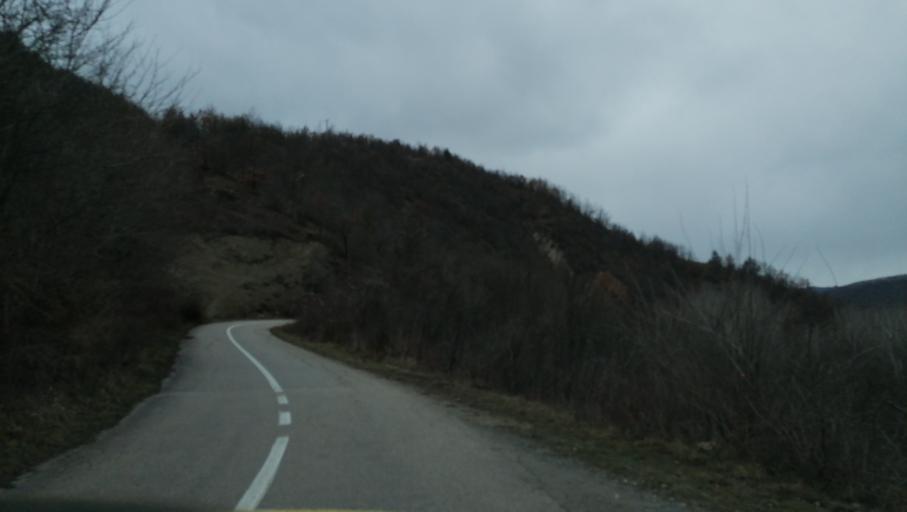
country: RS
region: Central Serbia
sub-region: Pirotski Okrug
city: Dimitrovgrad
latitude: 42.9535
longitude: 22.7802
